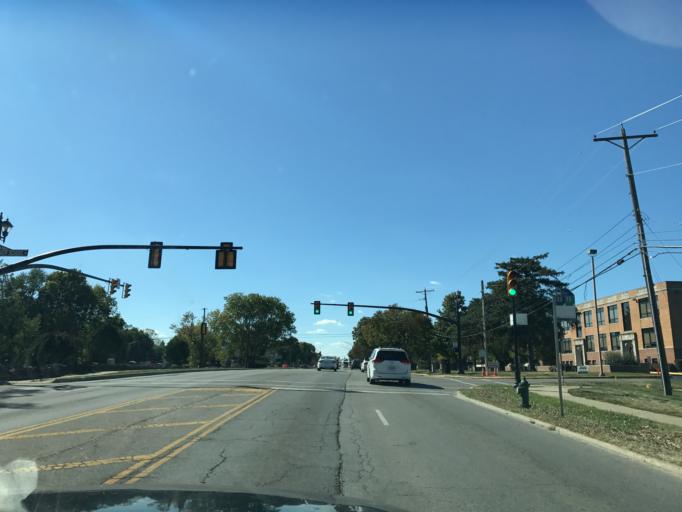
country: US
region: Ohio
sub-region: Franklin County
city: Dublin
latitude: 40.0993
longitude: -83.1167
